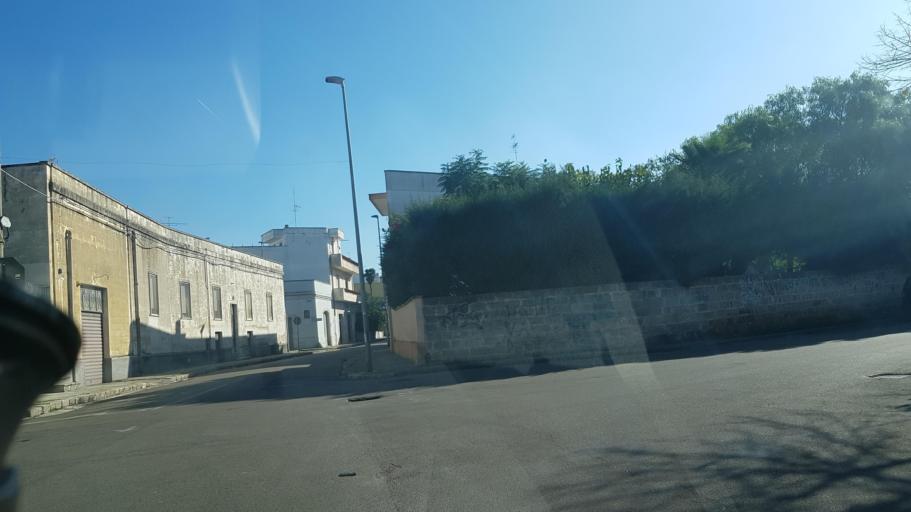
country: IT
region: Apulia
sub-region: Provincia di Lecce
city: Novoli
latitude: 40.3777
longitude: 18.0453
